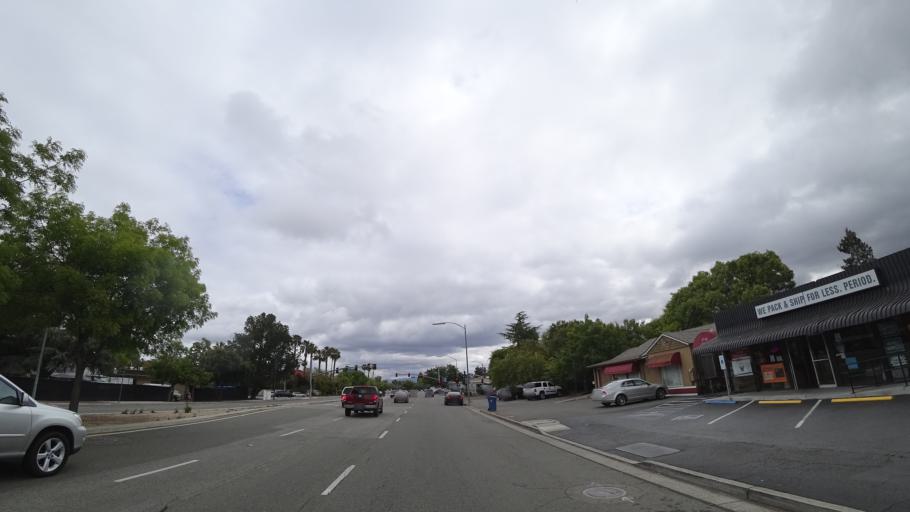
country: US
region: California
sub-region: Santa Clara County
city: Cambrian Park
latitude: 37.2716
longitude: -121.9363
